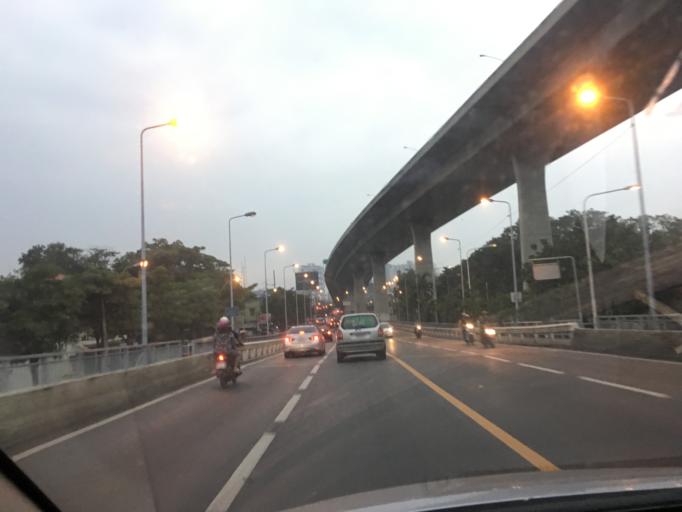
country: TH
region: Bangkok
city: Bang Kho Laem
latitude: 13.7019
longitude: 100.4904
